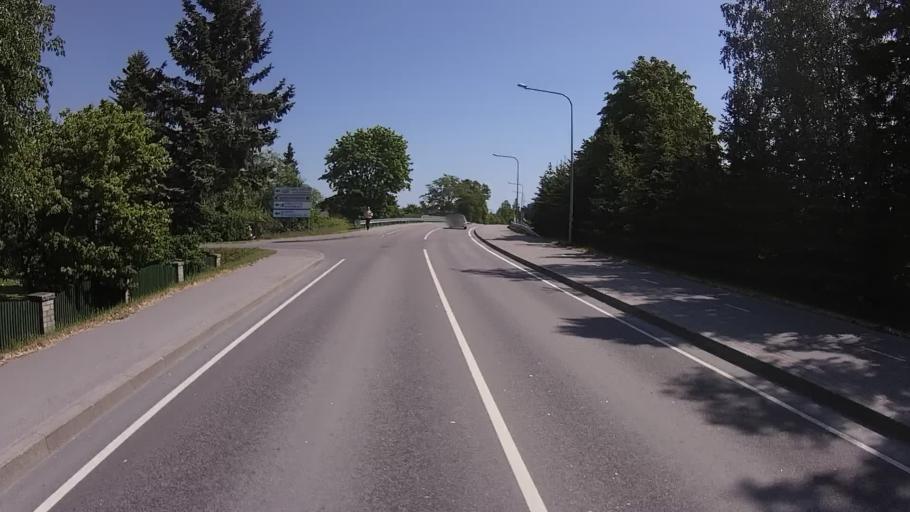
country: EE
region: Saare
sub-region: Kuressaare linn
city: Kuressaare
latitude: 58.2284
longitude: 22.3814
